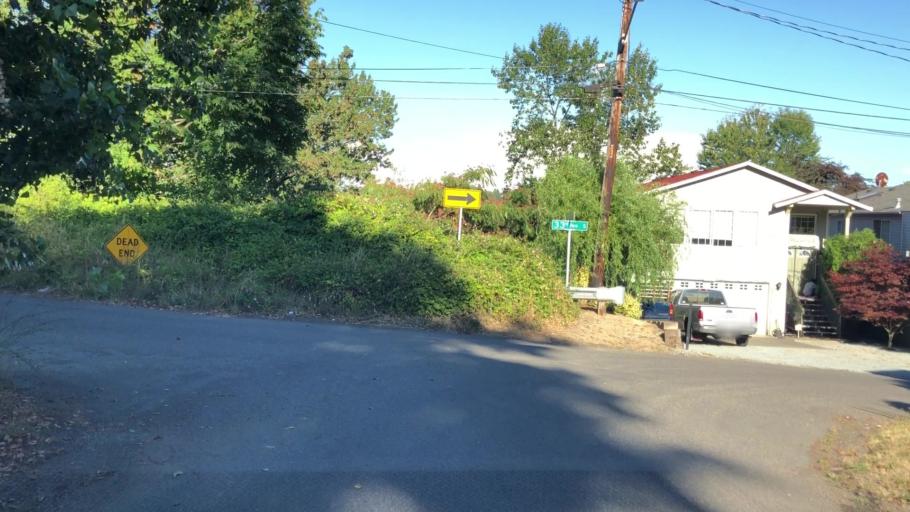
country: US
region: Washington
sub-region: King County
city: Boulevard Park
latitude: 47.5479
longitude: -122.2906
